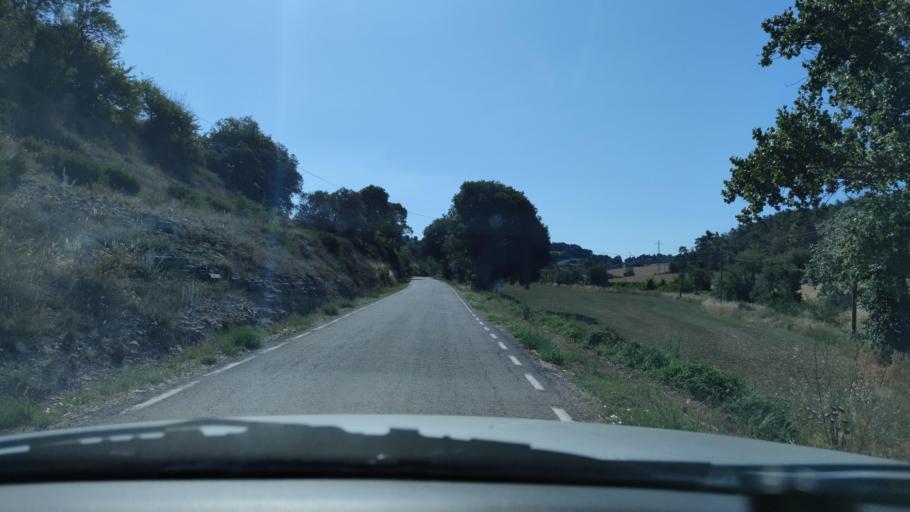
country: ES
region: Catalonia
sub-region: Provincia de Barcelona
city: Pujalt
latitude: 41.6872
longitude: 1.3917
